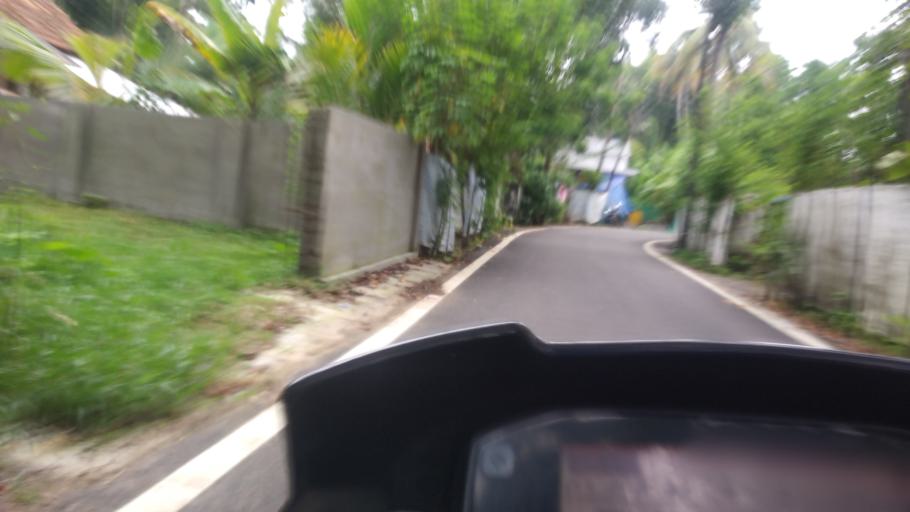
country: IN
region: Kerala
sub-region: Ernakulam
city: Elur
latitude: 10.0593
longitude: 76.2260
